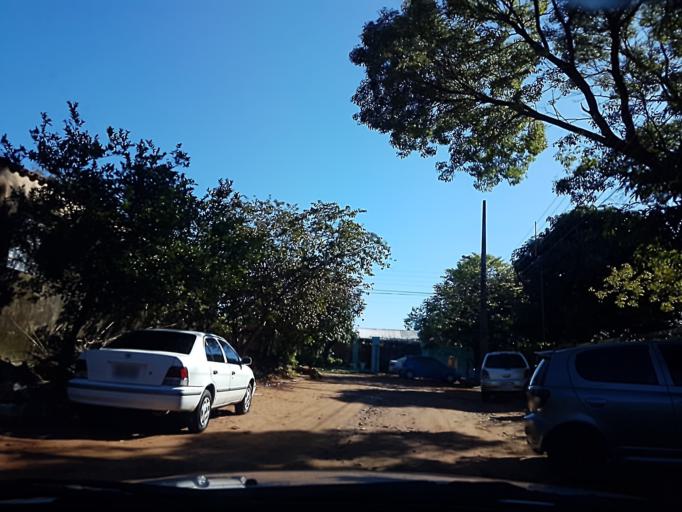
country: PY
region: Central
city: Nemby
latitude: -25.3972
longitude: -57.5425
